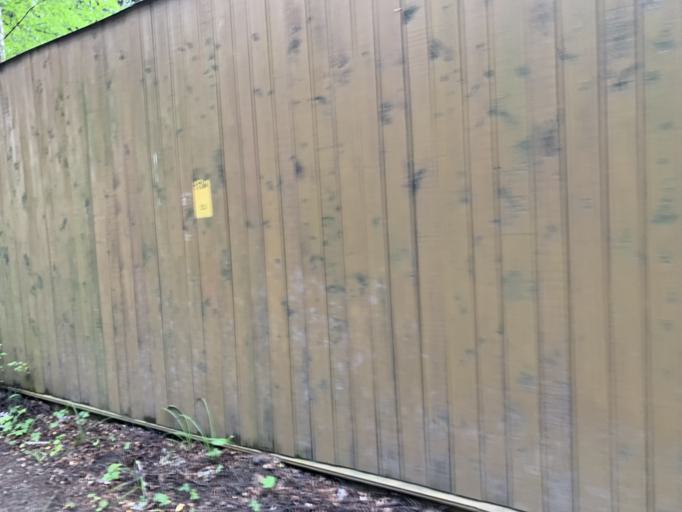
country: RU
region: Moskovskaya
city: Mamontovka
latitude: 55.9857
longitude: 37.8365
